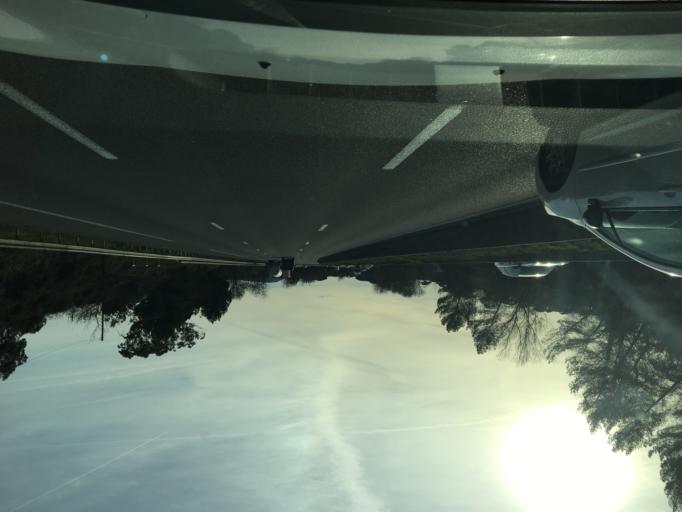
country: FR
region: Provence-Alpes-Cote d'Azur
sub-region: Departement du Var
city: Le Muy
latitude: 43.4646
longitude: 6.5725
